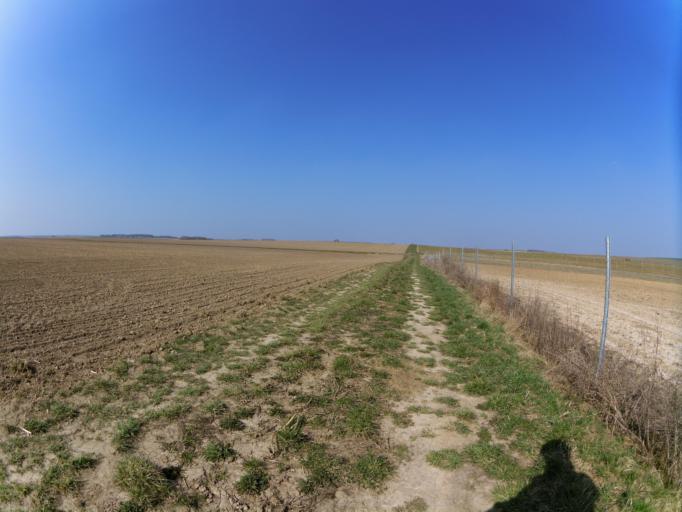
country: DE
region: Bavaria
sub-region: Regierungsbezirk Unterfranken
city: Giebelstadt
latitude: 49.6752
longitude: 9.9805
